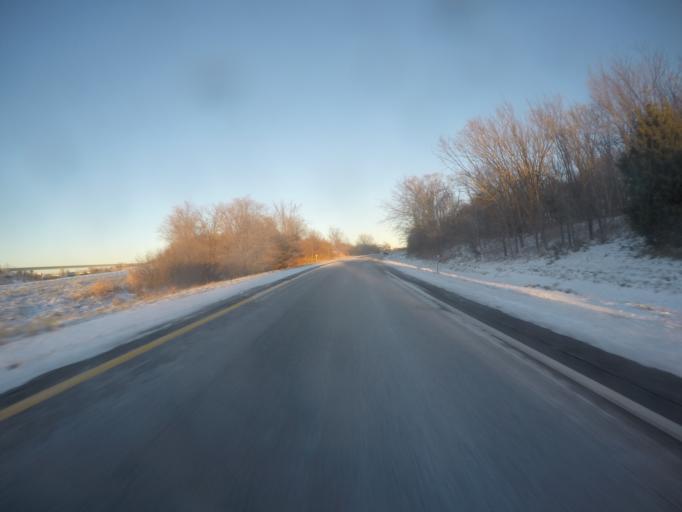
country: US
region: Missouri
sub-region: Platte County
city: Platte City
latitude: 39.3420
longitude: -94.7492
